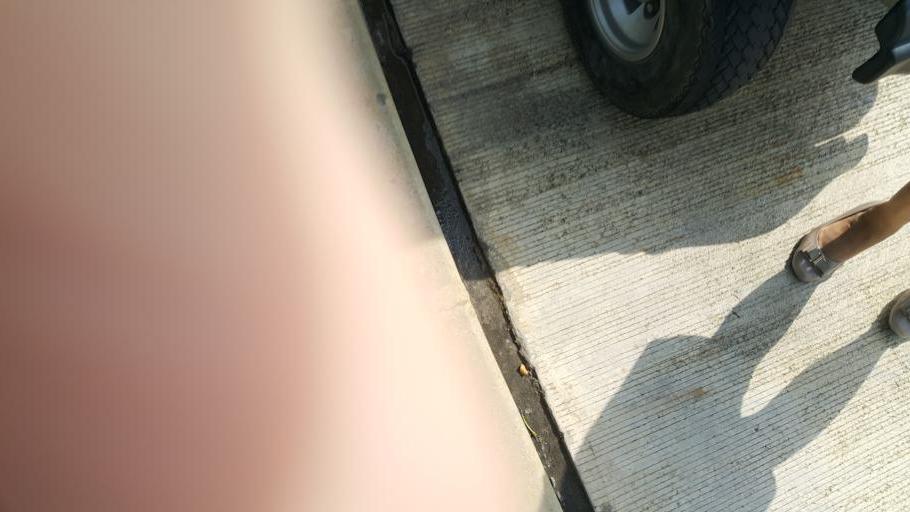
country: TH
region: Chiang Mai
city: San Kamphaeng
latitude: 18.7343
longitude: 99.0849
